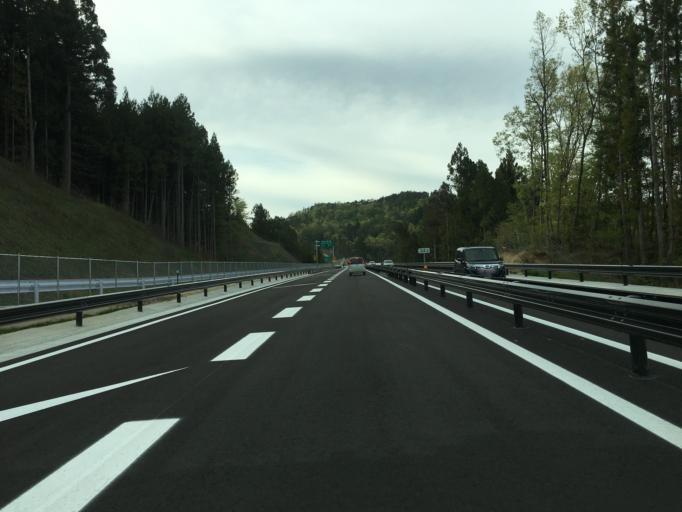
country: JP
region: Fukushima
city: Hobaramachi
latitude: 37.7741
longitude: 140.5837
